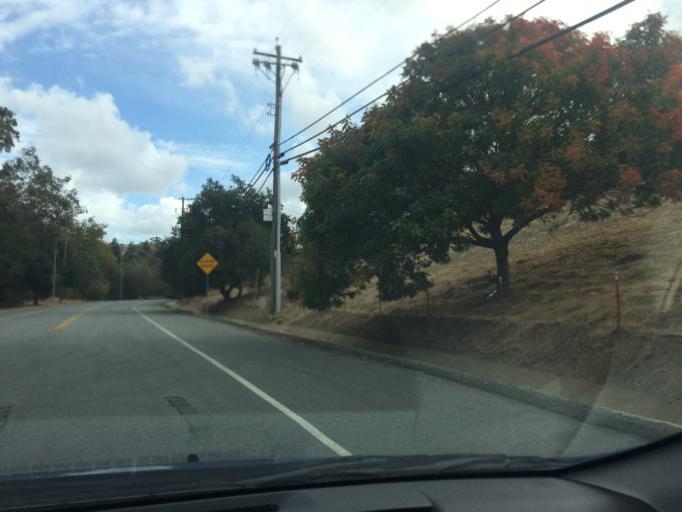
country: US
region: California
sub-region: Santa Clara County
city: Seven Trees
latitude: 37.2780
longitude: -121.7506
